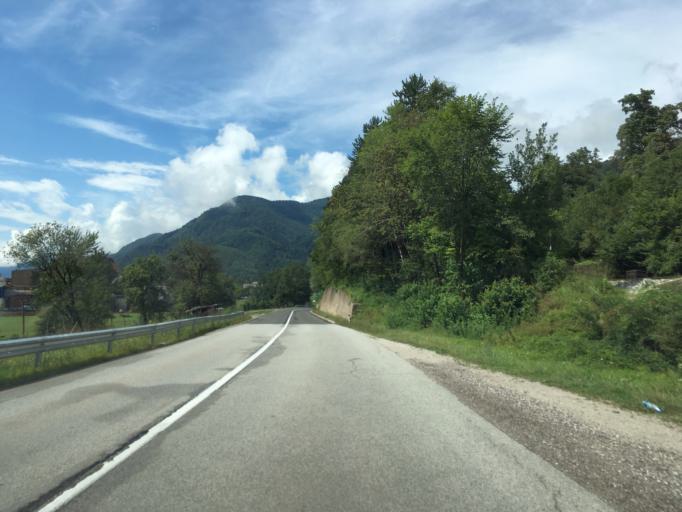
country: SI
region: Jesenice
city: Slovenski Javornik
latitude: 46.4189
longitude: 14.1081
